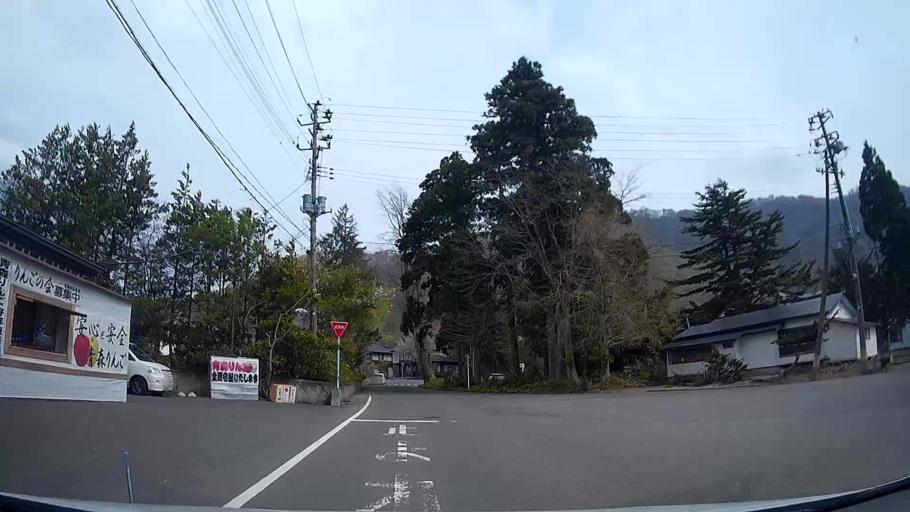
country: JP
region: Akita
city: Hanawa
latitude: 40.4259
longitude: 140.8968
